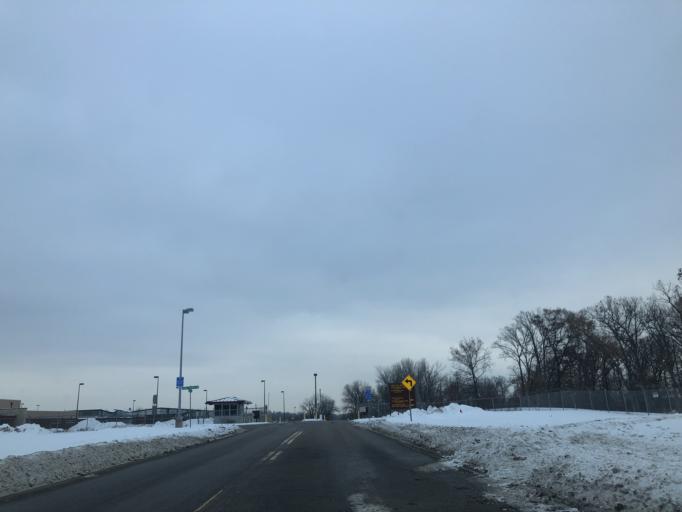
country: US
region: Minnesota
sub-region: Ramsey County
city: Shoreview
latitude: 45.0827
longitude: -93.1576
